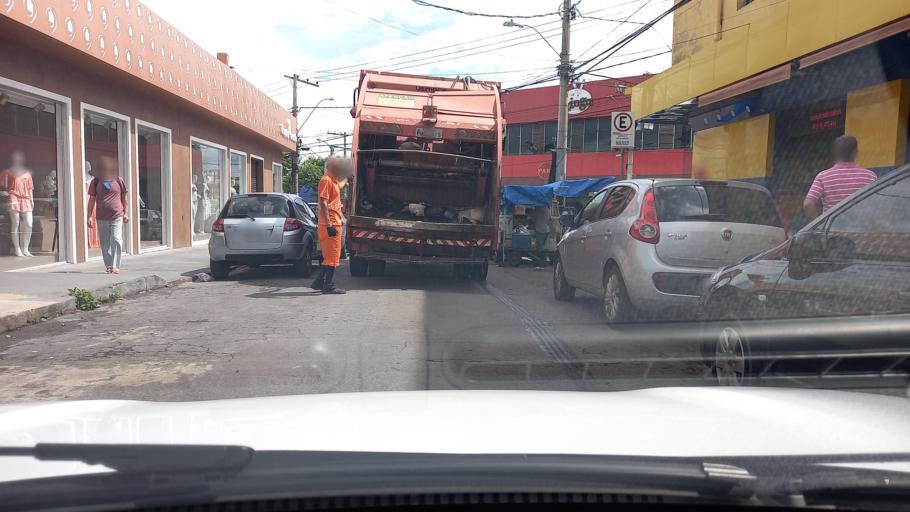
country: BR
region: Minas Gerais
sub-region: Contagem
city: Contagem
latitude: -19.9035
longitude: -44.0037
